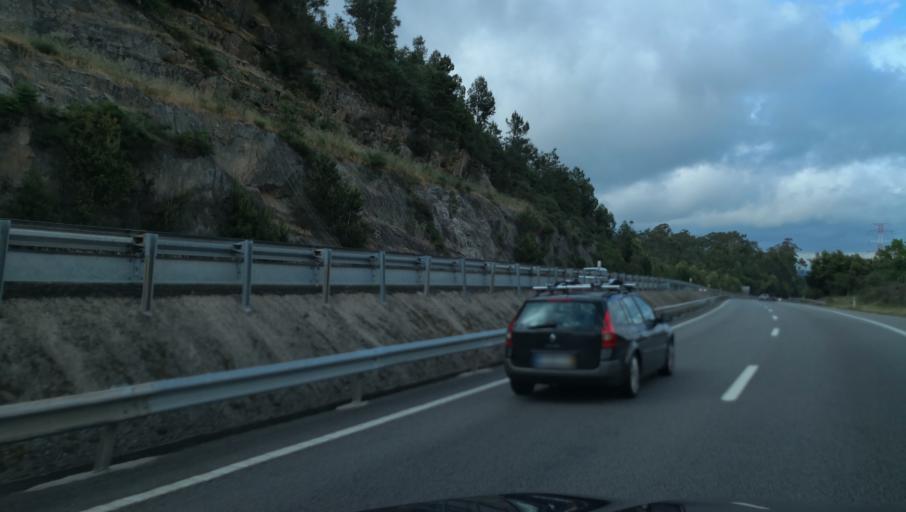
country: PT
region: Porto
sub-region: Paredes
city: Baltar
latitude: 41.1846
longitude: -8.3677
